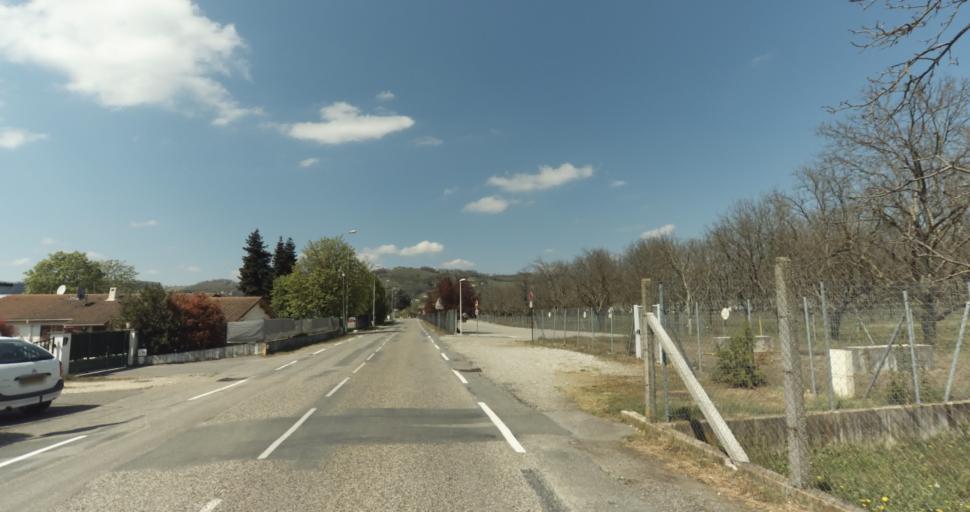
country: FR
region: Rhone-Alpes
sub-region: Departement de l'Isere
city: Saint-Marcellin
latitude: 45.1442
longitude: 5.3173
